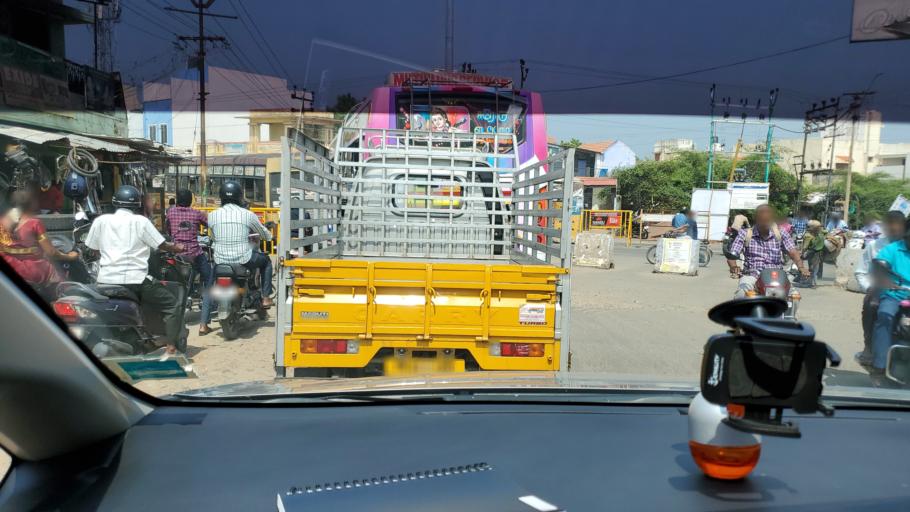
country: IN
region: Tamil Nadu
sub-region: Erode
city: Erode
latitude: 11.3506
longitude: 77.7225
